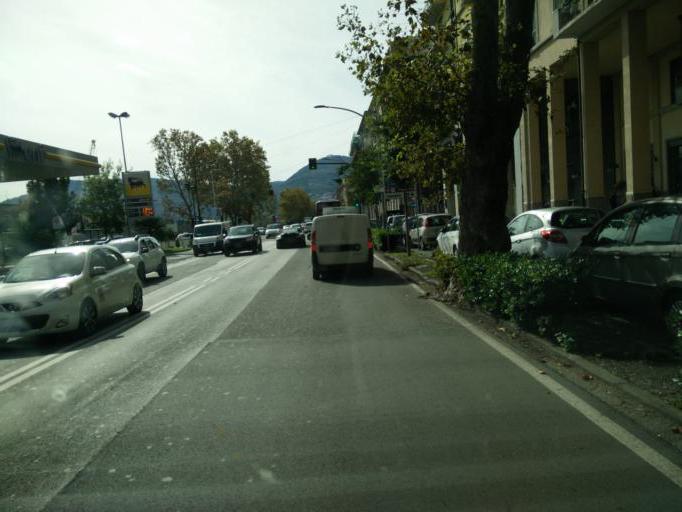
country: IT
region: Liguria
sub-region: Provincia di La Spezia
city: La Spezia
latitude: 44.1111
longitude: 9.8347
